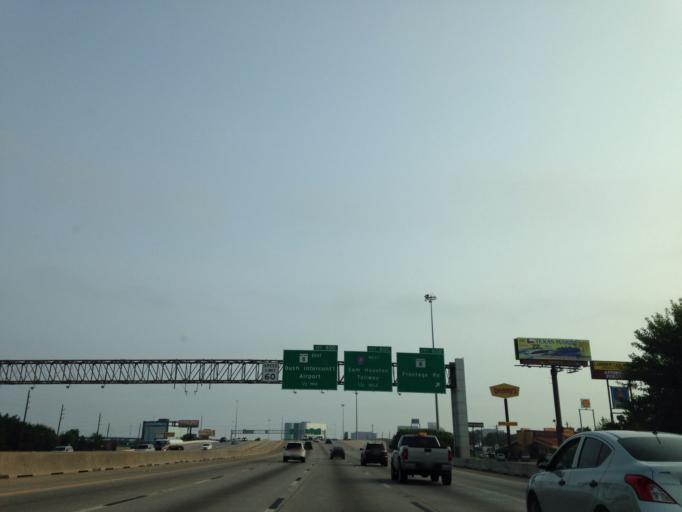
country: US
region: Texas
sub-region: Harris County
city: Aldine
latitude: 29.9285
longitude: -95.4118
